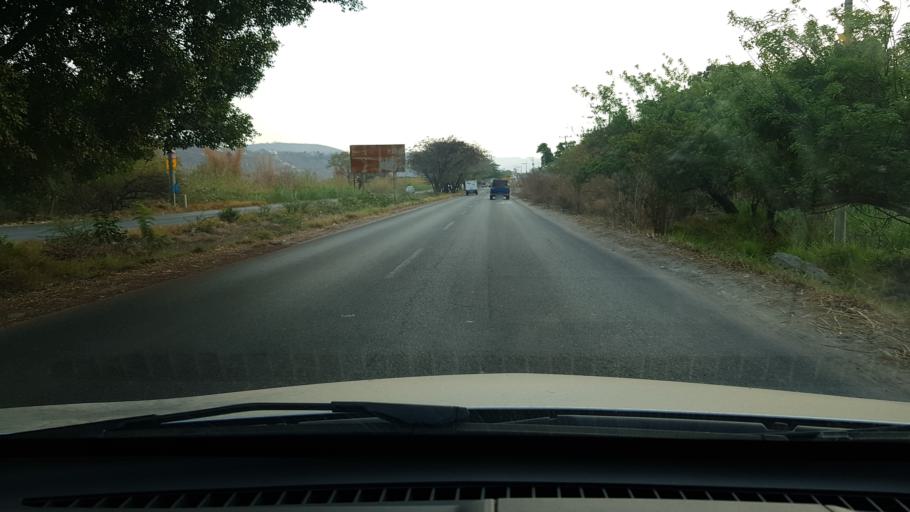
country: MX
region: Morelos
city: Yautepec
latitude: 18.8773
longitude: -99.0543
